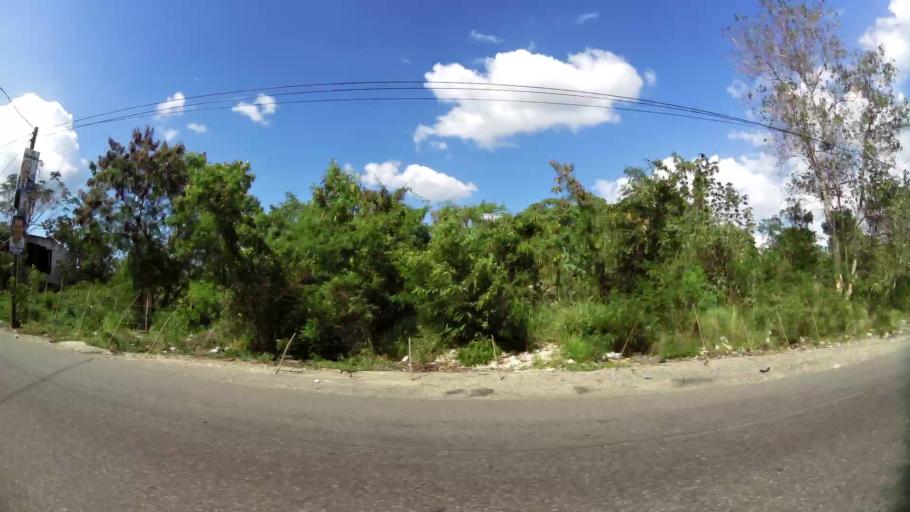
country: DO
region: San Cristobal
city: Bajos de Haina
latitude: 18.4273
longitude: -70.0587
